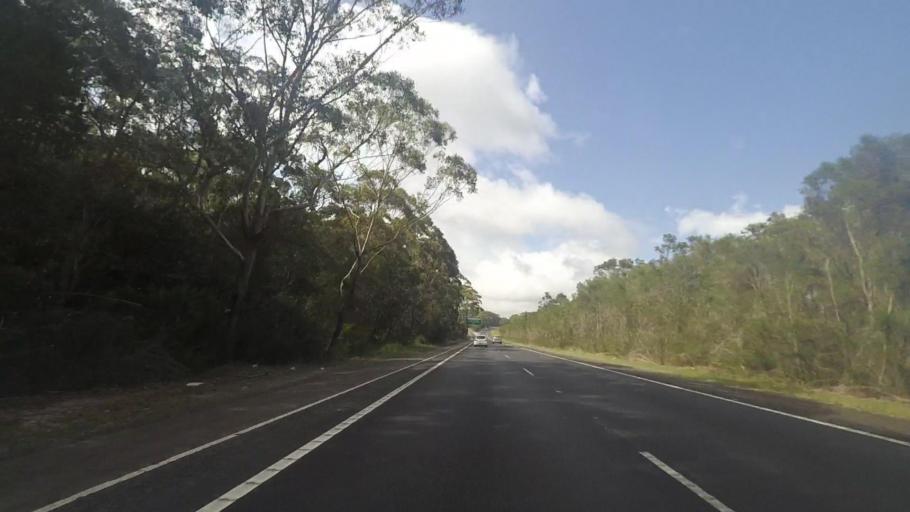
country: AU
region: New South Wales
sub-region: Wollongong
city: Helensburgh
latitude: -34.1966
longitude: 150.9663
